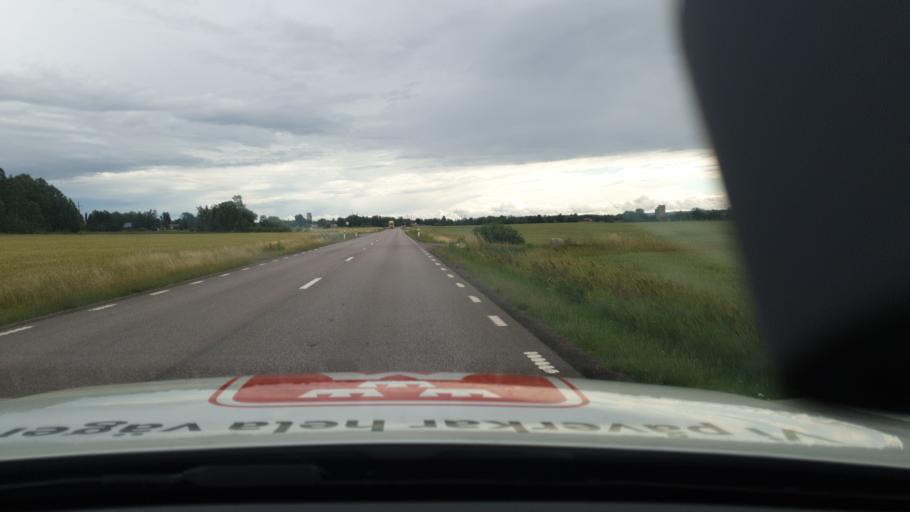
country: SE
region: Vaestra Goetaland
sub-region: Toreboda Kommun
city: Toereboda
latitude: 58.5926
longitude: 14.0074
